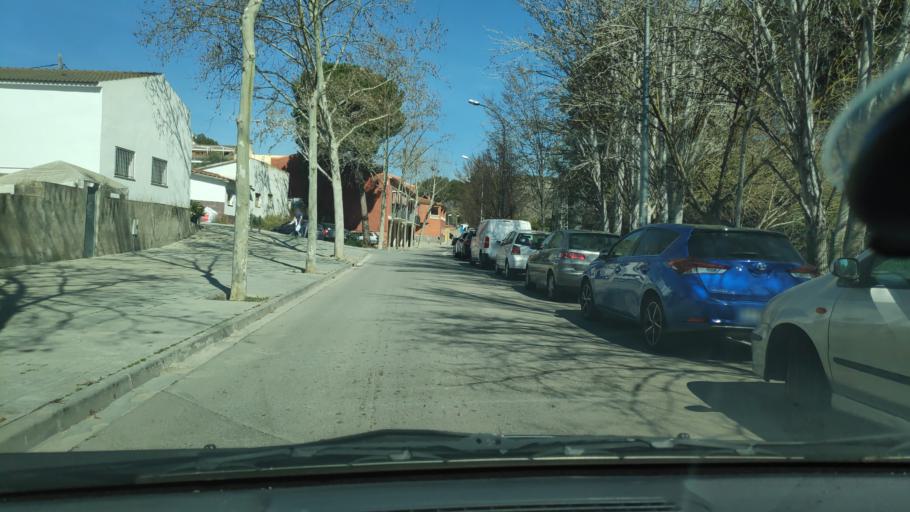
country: ES
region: Catalonia
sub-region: Provincia de Barcelona
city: Rubi
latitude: 41.4994
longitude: 2.0462
